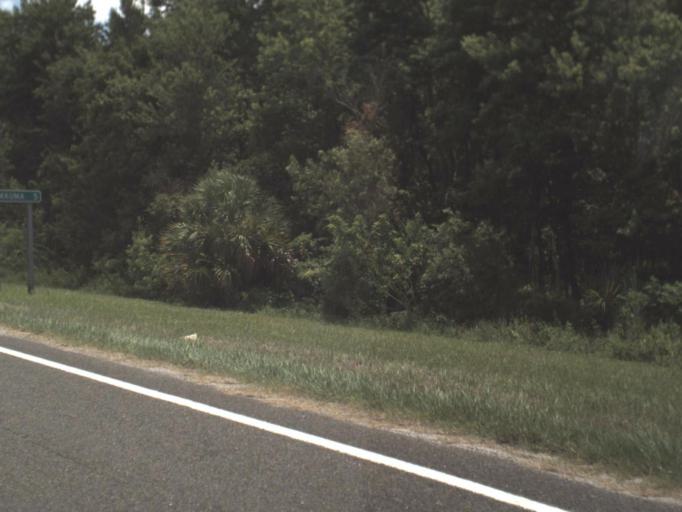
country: US
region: Florida
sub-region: Hillsborough County
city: Sun City Center
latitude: 27.7122
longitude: -82.3744
